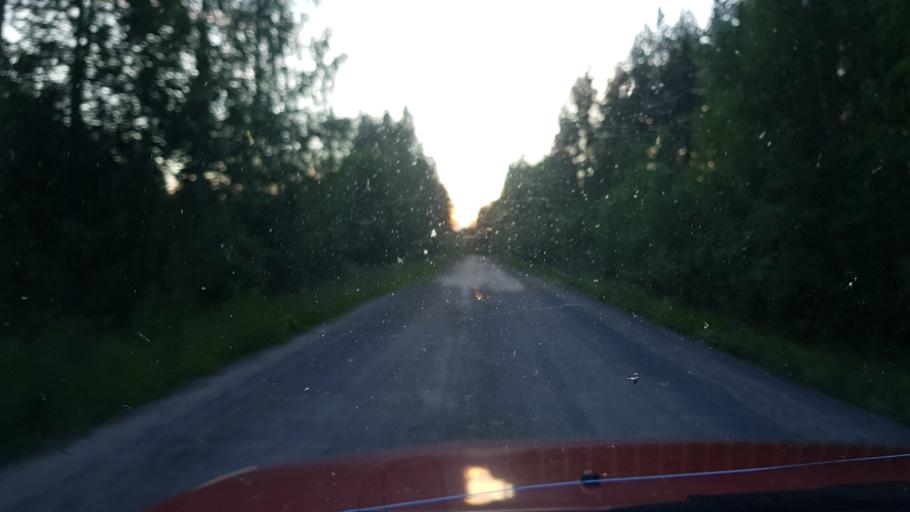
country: SE
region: Norrbotten
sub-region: Alvsbyns Kommun
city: AElvsbyn
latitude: 65.6946
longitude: 20.6721
